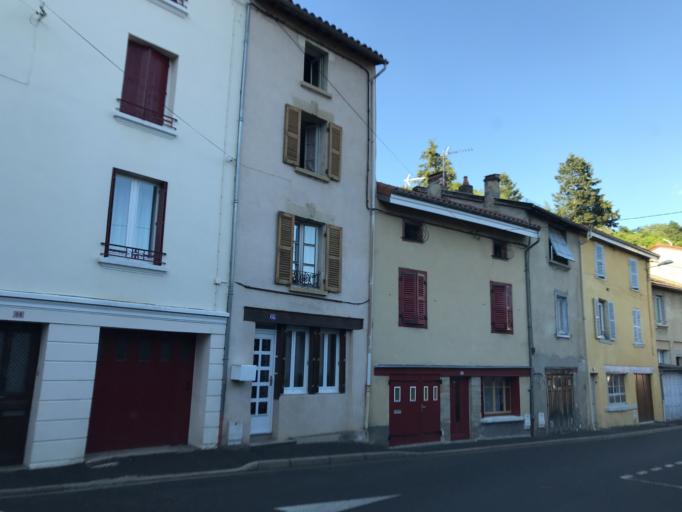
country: FR
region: Auvergne
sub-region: Departement du Puy-de-Dome
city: Thiers
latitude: 45.8608
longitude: 3.5499
